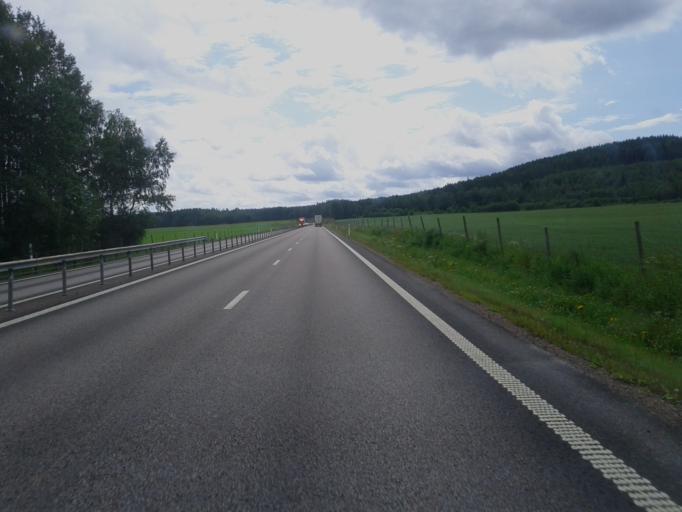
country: SE
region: Dalarna
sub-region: Borlange Kommun
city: Ornas
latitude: 60.4009
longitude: 15.6138
